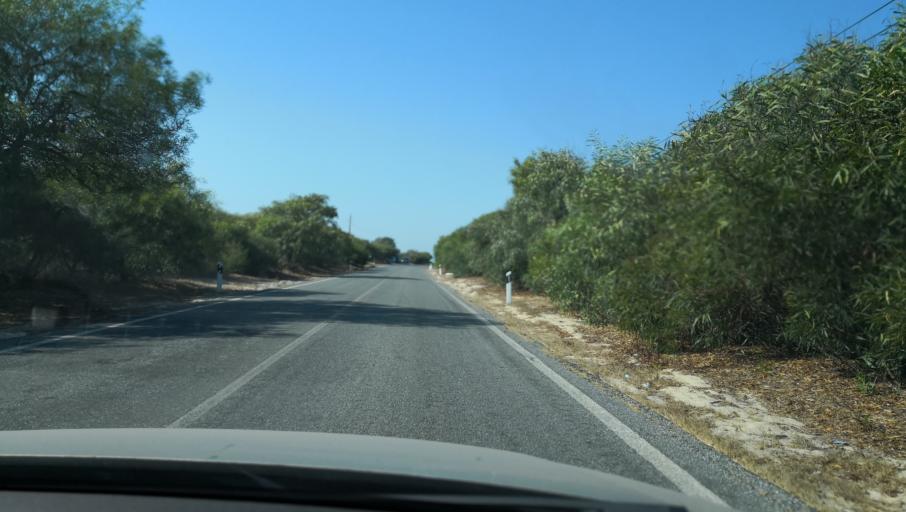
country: PT
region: Setubal
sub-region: Setubal
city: Setubal
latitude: 38.3905
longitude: -8.8012
